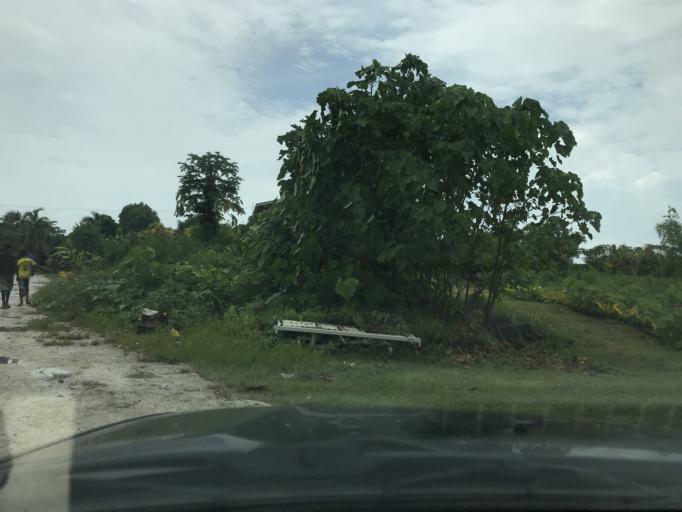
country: SB
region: Western Province
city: Gizo
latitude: -8.3298
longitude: 157.2504
